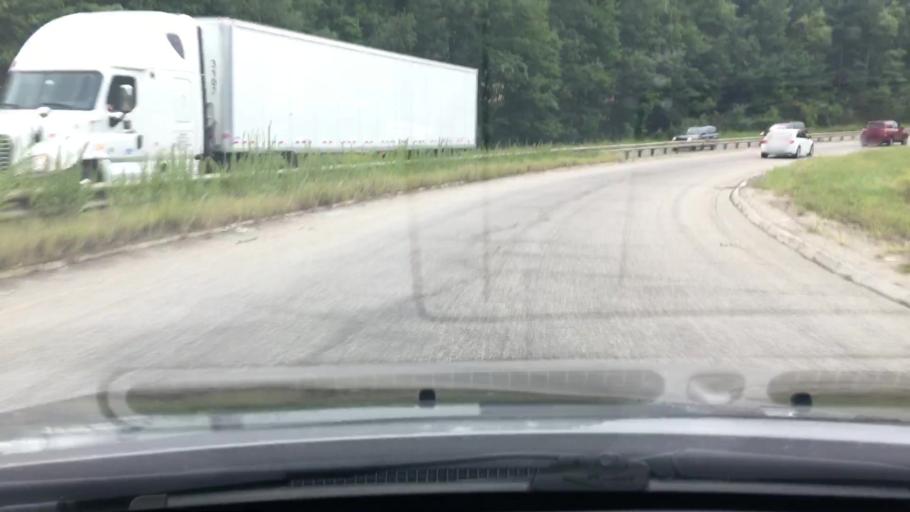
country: US
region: Massachusetts
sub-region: Worcester County
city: Cordaville
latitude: 42.2641
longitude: -71.5612
